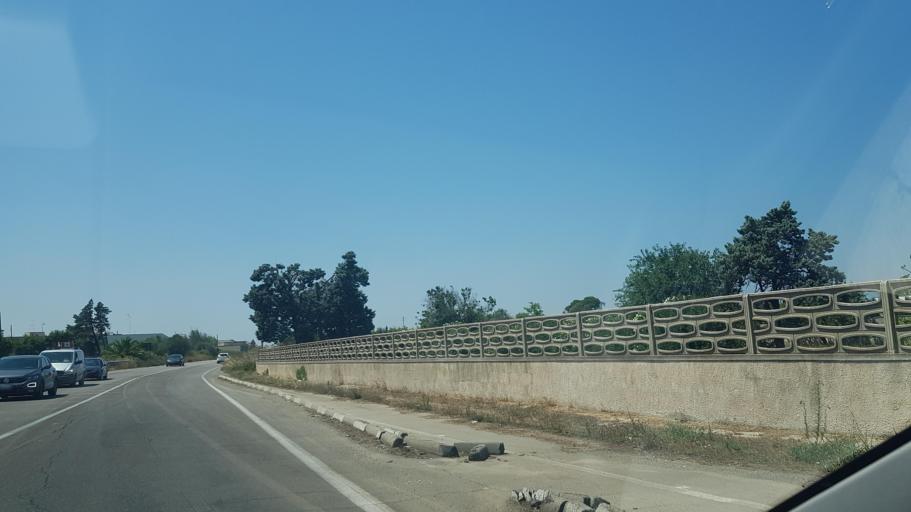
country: IT
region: Apulia
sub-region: Provincia di Lecce
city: Vernole
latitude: 40.2902
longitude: 18.3088
